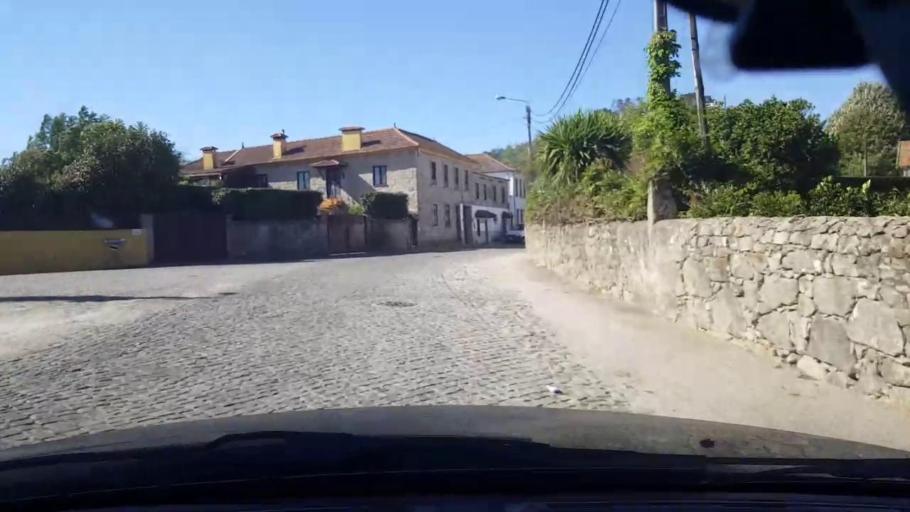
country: PT
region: Porto
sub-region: Maia
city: Gemunde
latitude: 41.2921
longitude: -8.6364
